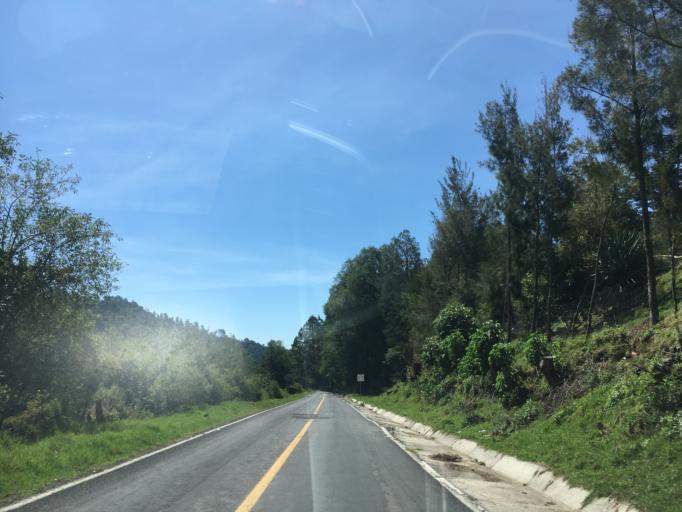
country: MX
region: Michoacan
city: Tzitzio
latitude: 19.6625
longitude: -100.8059
